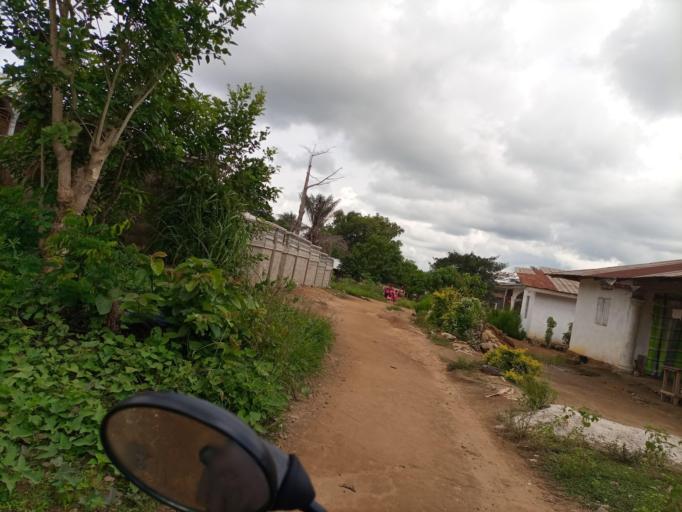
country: SL
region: Southern Province
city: Bo
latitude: 7.9728
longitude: -11.7668
